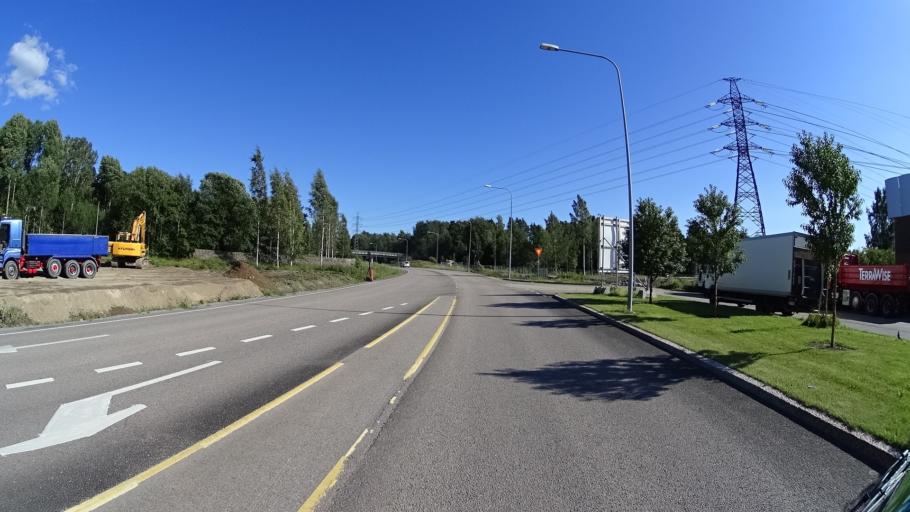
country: FI
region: Uusimaa
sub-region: Helsinki
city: Vantaa
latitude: 60.2328
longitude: 25.1117
